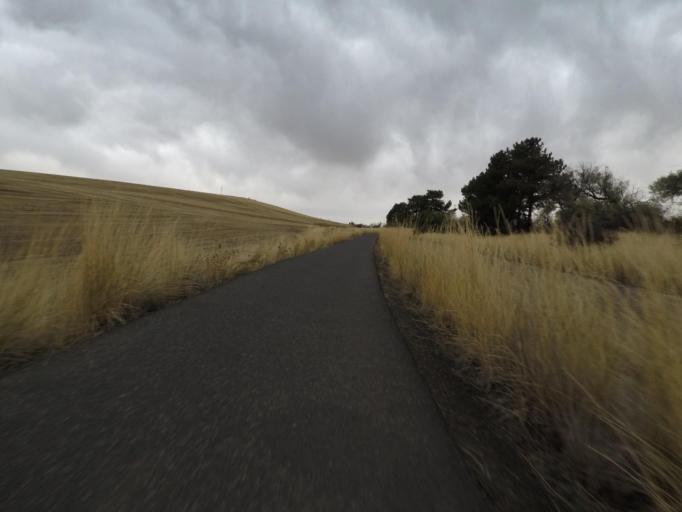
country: US
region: Washington
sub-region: Walla Walla County
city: Walla Walla East
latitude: 46.0697
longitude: -118.2698
